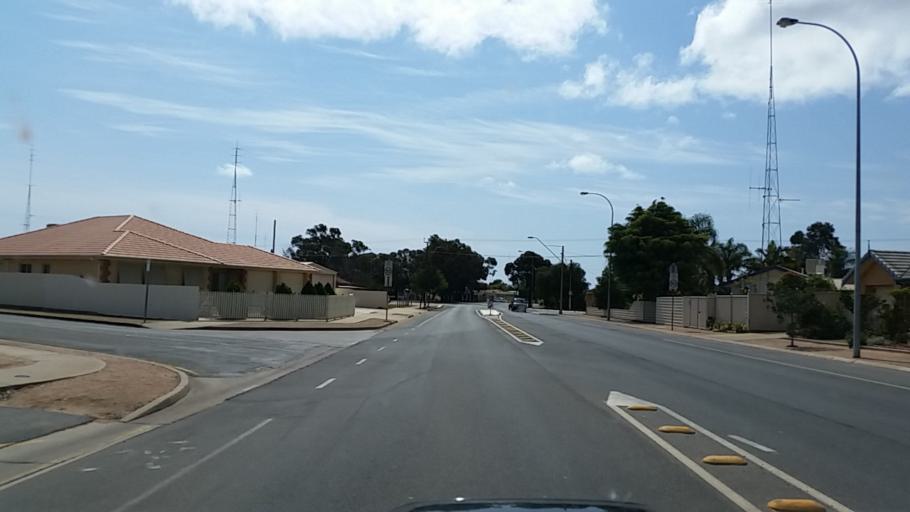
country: AU
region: South Australia
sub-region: Port Pirie City and Dists
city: Port Pirie
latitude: -33.2048
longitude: 138.0115
